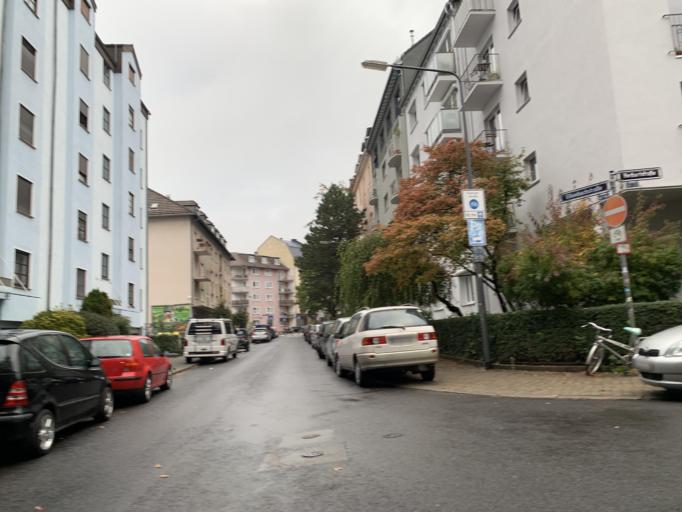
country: DE
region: Hesse
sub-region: Regierungsbezirk Darmstadt
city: Frankfurt am Main
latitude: 50.1217
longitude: 8.6948
